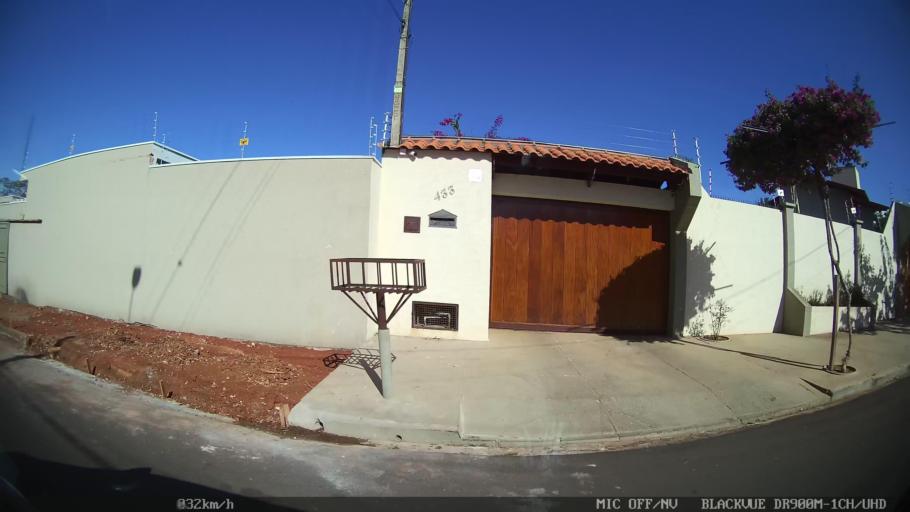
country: BR
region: Sao Paulo
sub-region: Olimpia
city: Olimpia
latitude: -20.7324
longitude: -48.9174
